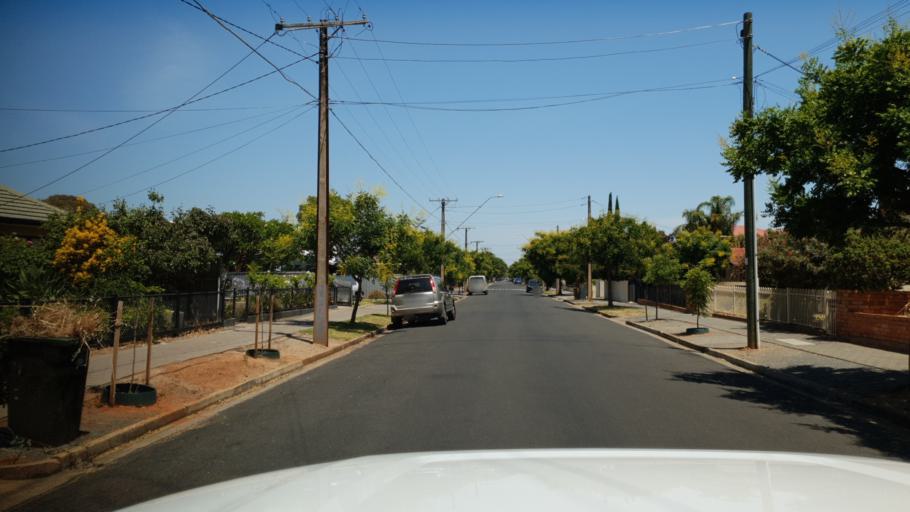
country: AU
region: South Australia
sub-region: Mitcham
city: Clapham
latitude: -34.9879
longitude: 138.5895
